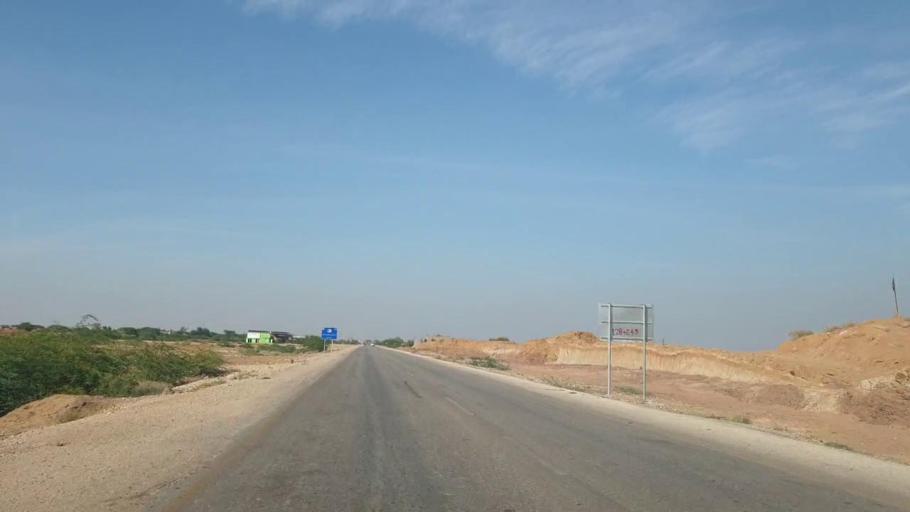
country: PK
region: Sindh
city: Sehwan
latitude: 26.3740
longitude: 67.8736
